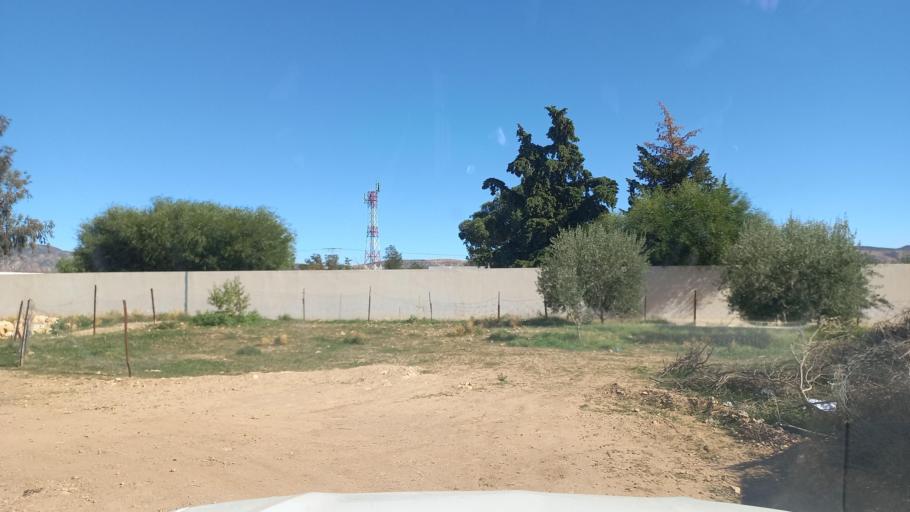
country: TN
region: Al Qasrayn
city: Sbiba
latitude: 35.3950
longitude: 9.1184
